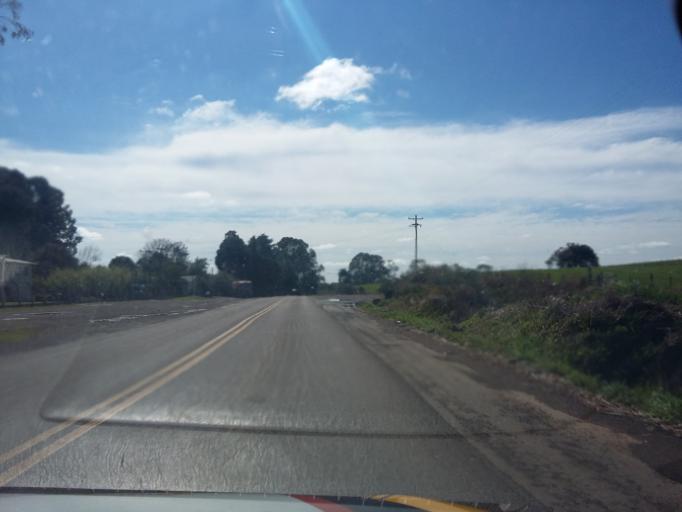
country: BR
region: Rio Grande do Sul
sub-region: Sao Marcos
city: Sao Marcos
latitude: -28.7177
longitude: -51.0875
